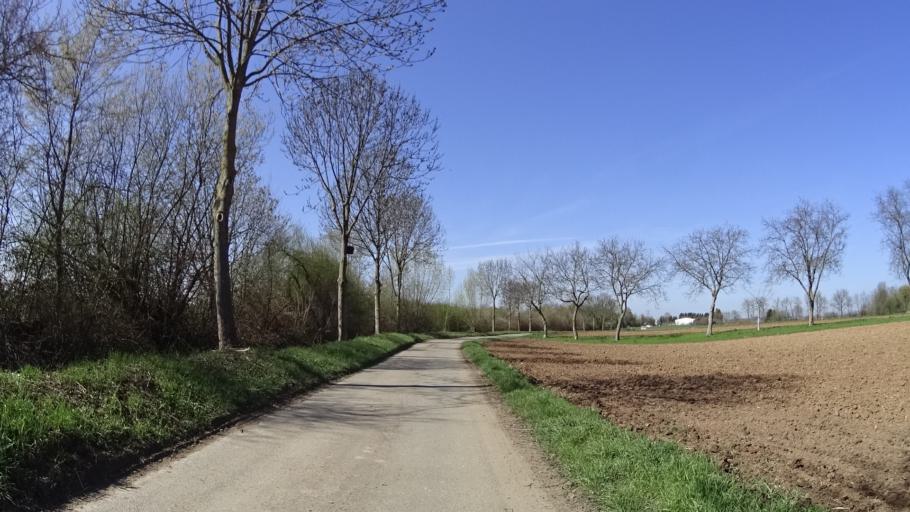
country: DE
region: Baden-Wuerttemberg
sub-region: Karlsruhe Region
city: Dossenheim
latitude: 49.4509
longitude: 8.6528
